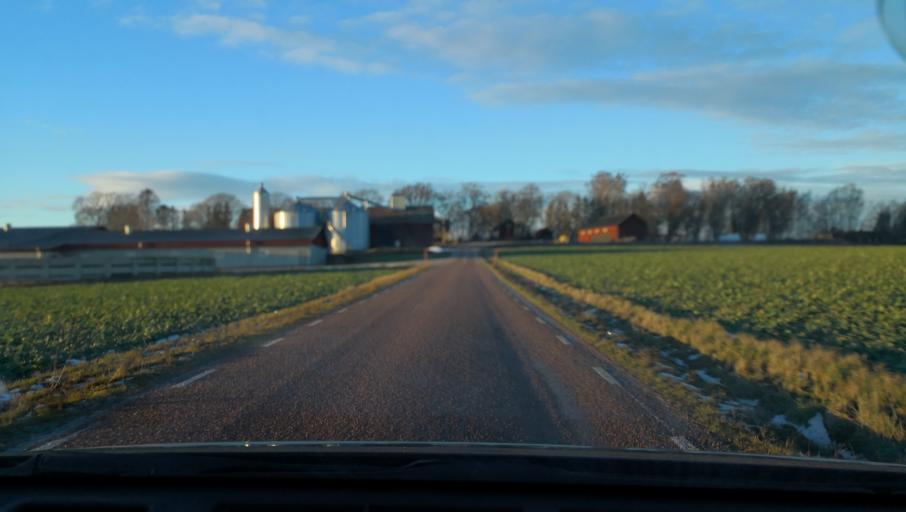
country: SE
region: Vaestmanland
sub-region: Vasteras
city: Hokasen
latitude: 59.7002
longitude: 16.5840
